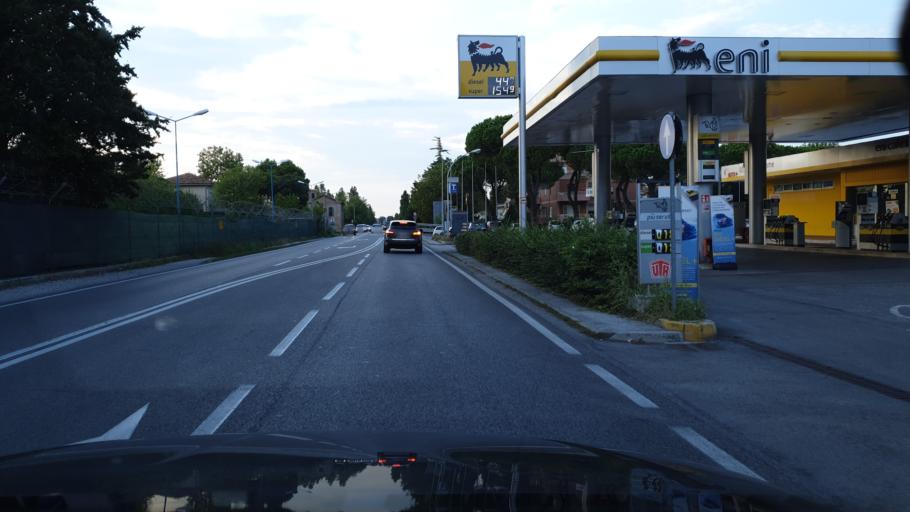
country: IT
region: Emilia-Romagna
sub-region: Provincia di Rimini
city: Rivazzurra
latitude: 44.0260
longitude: 12.6156
